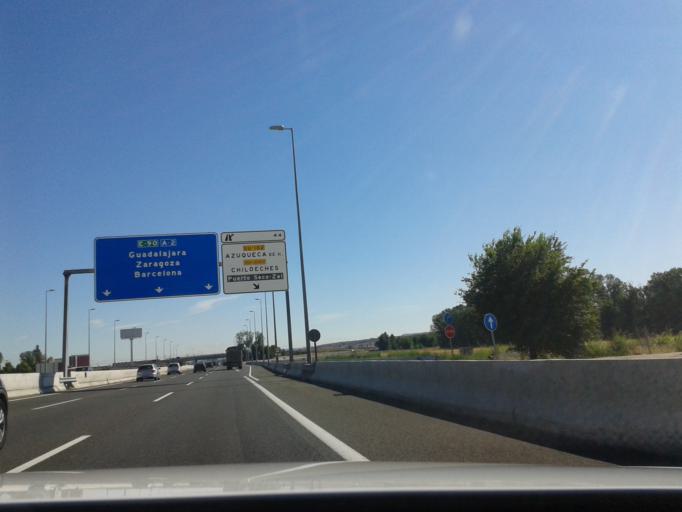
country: ES
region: Castille-La Mancha
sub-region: Provincia de Guadalajara
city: Azuqueca de Henares
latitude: 40.5657
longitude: -3.2507
